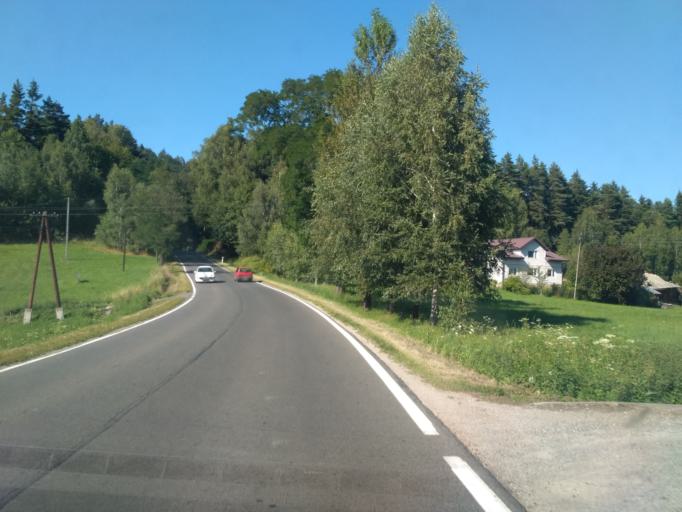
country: PL
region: Subcarpathian Voivodeship
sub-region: Powiat krosnienski
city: Korczyna
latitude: 49.7383
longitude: 21.8082
